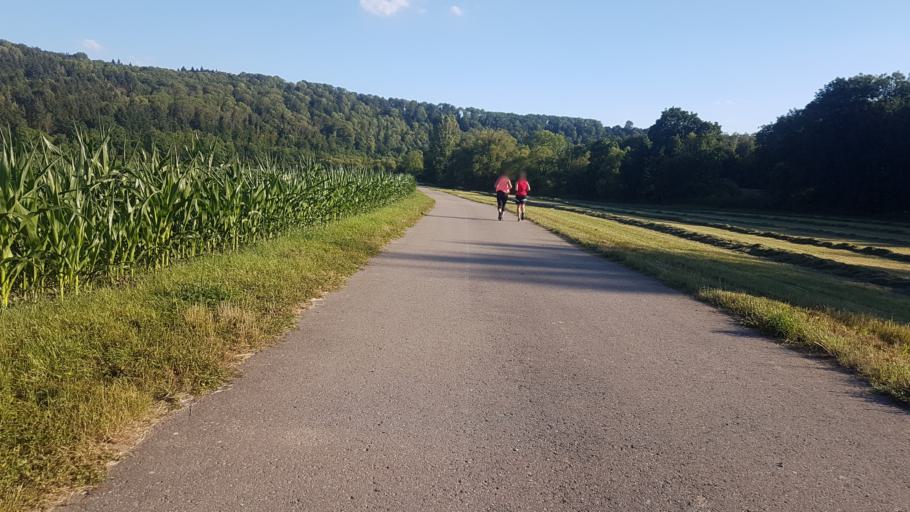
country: DE
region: Baden-Wuerttemberg
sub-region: Regierungsbezirk Stuttgart
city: Neudenau
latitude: 49.2931
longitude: 9.2981
